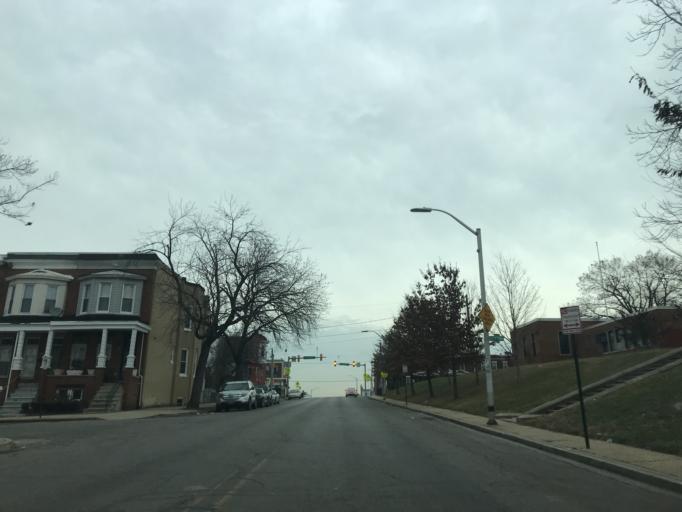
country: US
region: Maryland
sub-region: City of Baltimore
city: Baltimore
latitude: 39.3063
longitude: -76.6554
